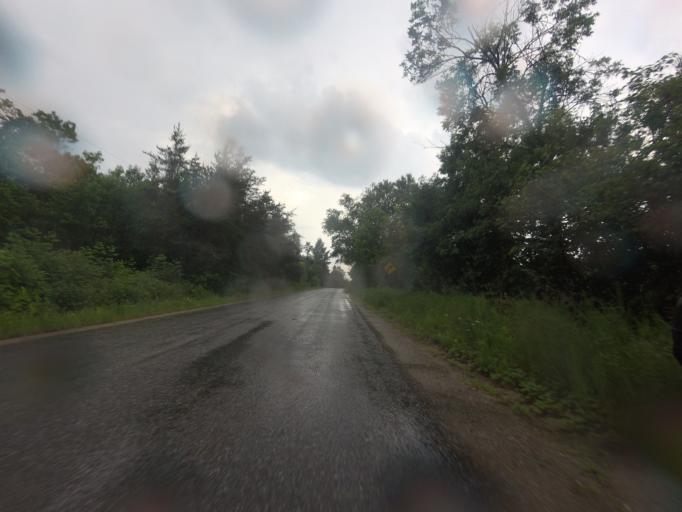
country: CA
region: Quebec
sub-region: Outaouais
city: Maniwaki
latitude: 46.4075
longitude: -75.9592
